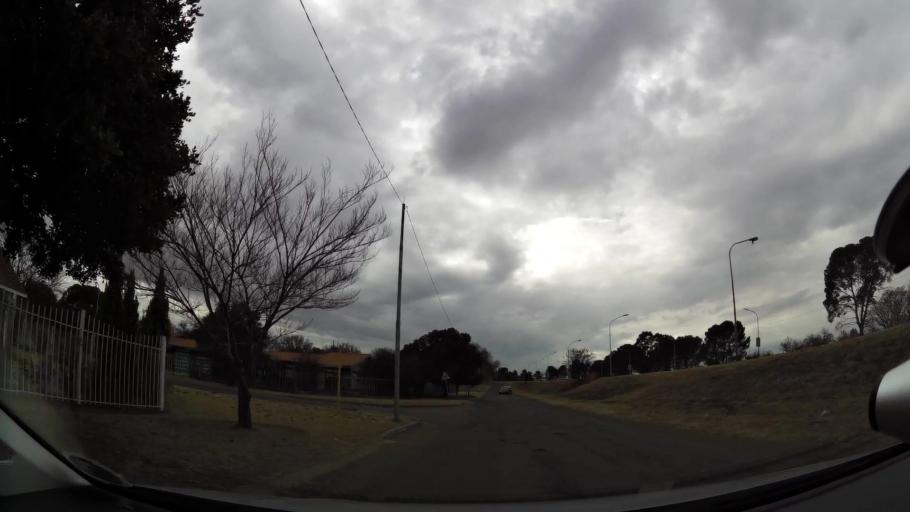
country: ZA
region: Orange Free State
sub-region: Fezile Dabi District Municipality
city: Kroonstad
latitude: -27.6416
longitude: 27.2330
